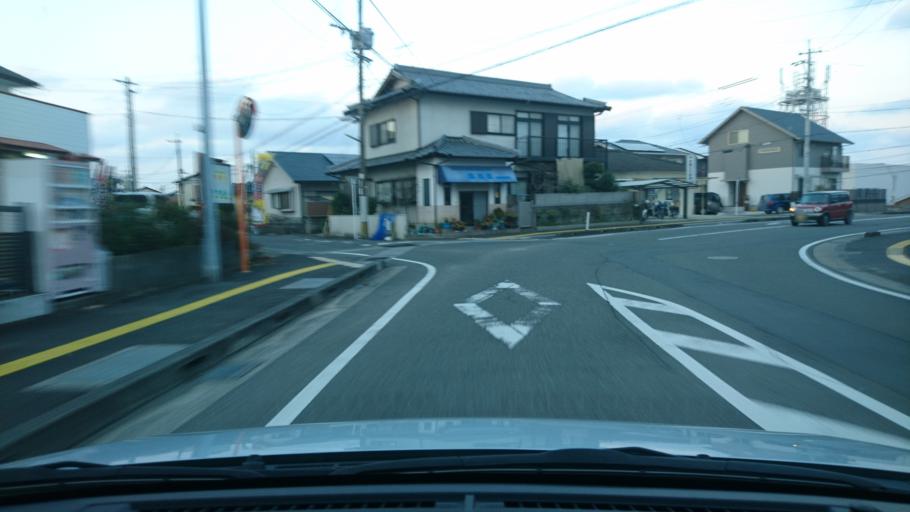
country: JP
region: Miyazaki
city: Miyazaki-shi
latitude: 31.8606
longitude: 131.4286
